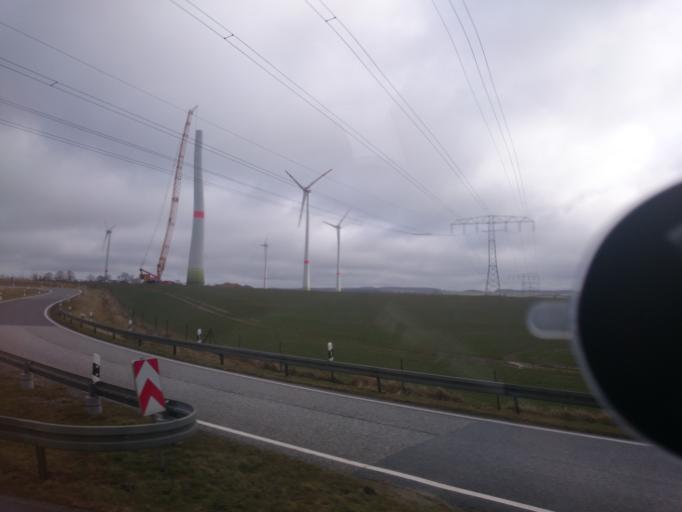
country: DE
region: Mecklenburg-Vorpommern
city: Muhl Rosin
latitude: 53.8249
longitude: 12.3005
